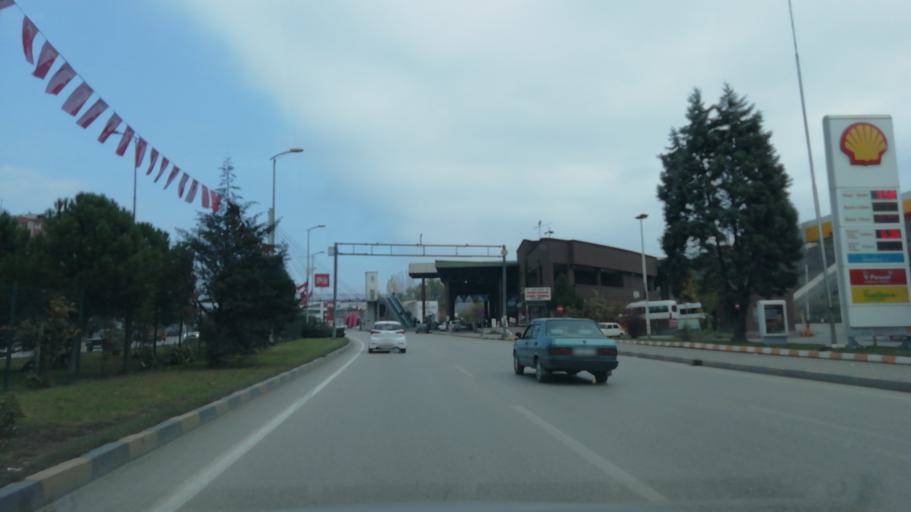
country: TR
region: Karabuk
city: Karabuk
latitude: 41.1959
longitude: 32.6240
